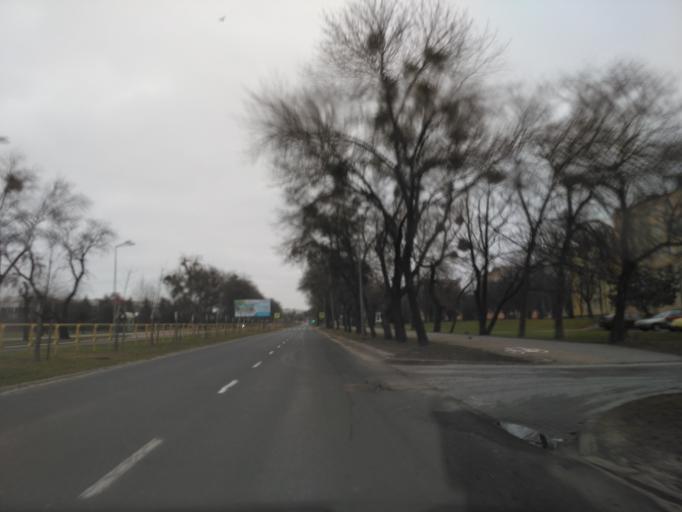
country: PL
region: Lublin Voivodeship
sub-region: Chelm
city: Chelm
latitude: 51.1283
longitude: 23.4750
